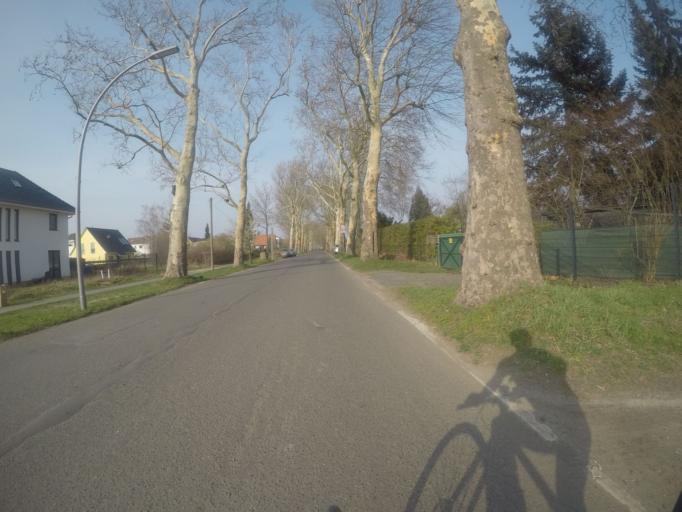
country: DE
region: Berlin
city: Rudow
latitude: 52.3994
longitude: 13.4877
